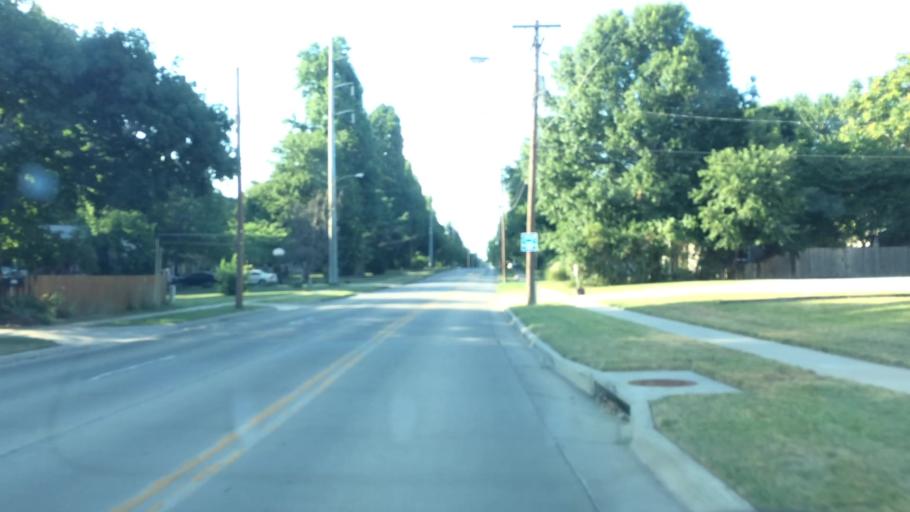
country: US
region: Missouri
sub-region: Greene County
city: Springfield
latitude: 37.1897
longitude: -93.2903
